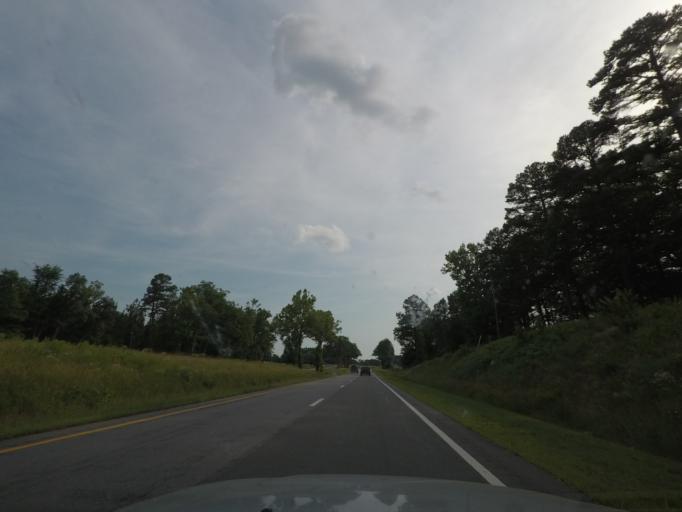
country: US
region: Virginia
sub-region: Mecklenburg County
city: Chase City
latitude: 36.8782
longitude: -78.5626
